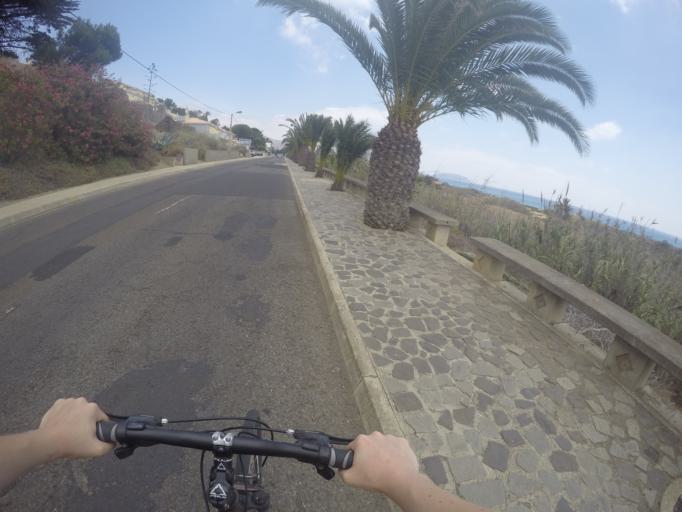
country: PT
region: Madeira
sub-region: Porto Santo
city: Vila de Porto Santo
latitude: 33.0524
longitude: -16.3487
